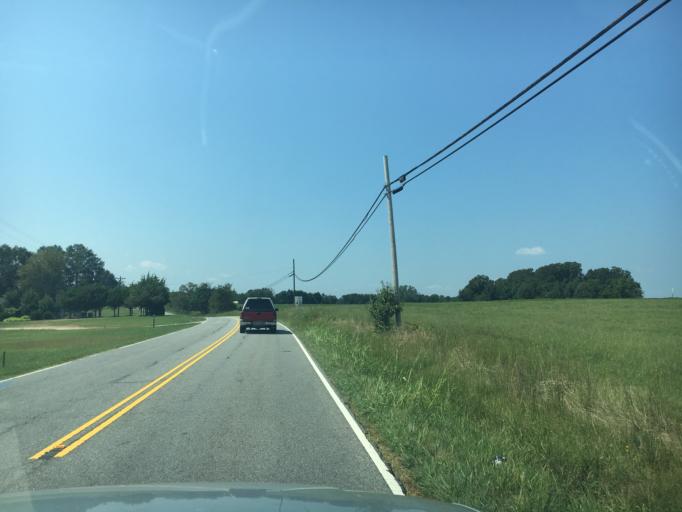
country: US
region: South Carolina
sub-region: Anderson County
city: Centerville
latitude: 34.5191
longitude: -82.7352
